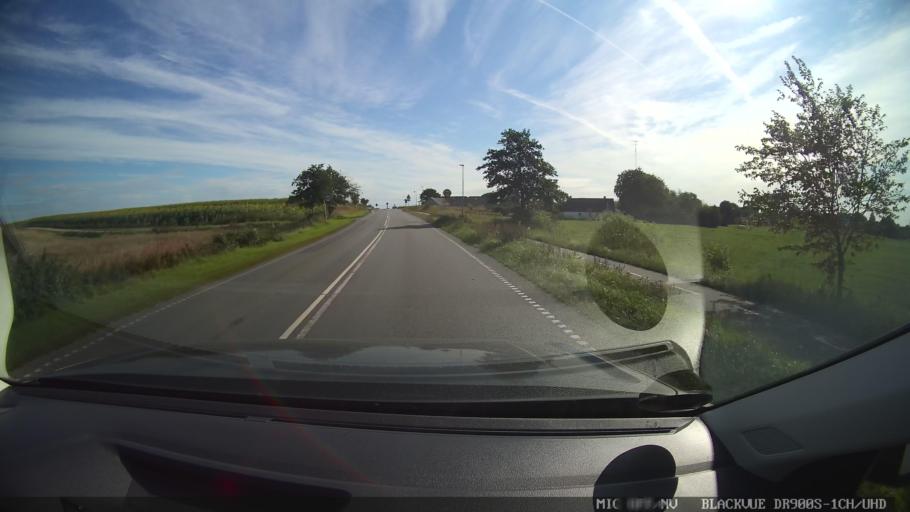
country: DK
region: North Denmark
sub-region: Mariagerfjord Kommune
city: Arden
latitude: 56.7636
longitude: 9.8780
